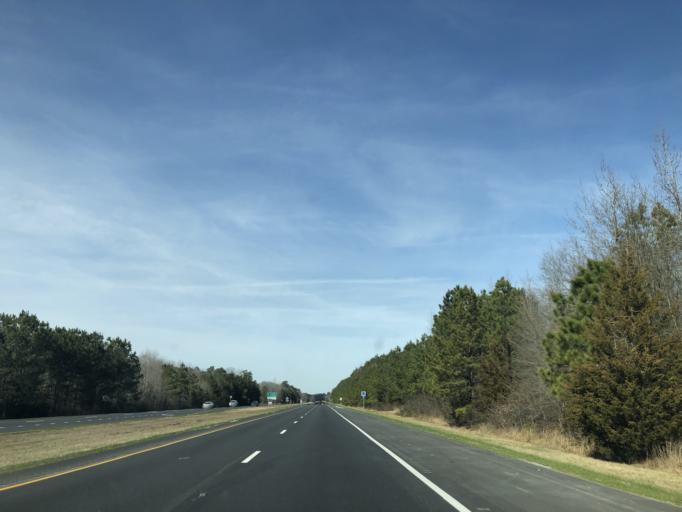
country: US
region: Delaware
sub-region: Sussex County
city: Georgetown
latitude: 38.7397
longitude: -75.4242
